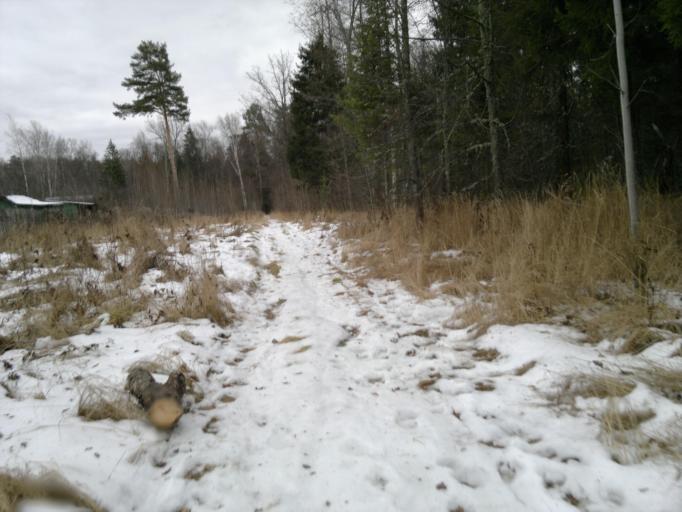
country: RU
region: Mariy-El
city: Yoshkar-Ola
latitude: 56.6104
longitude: 47.9538
